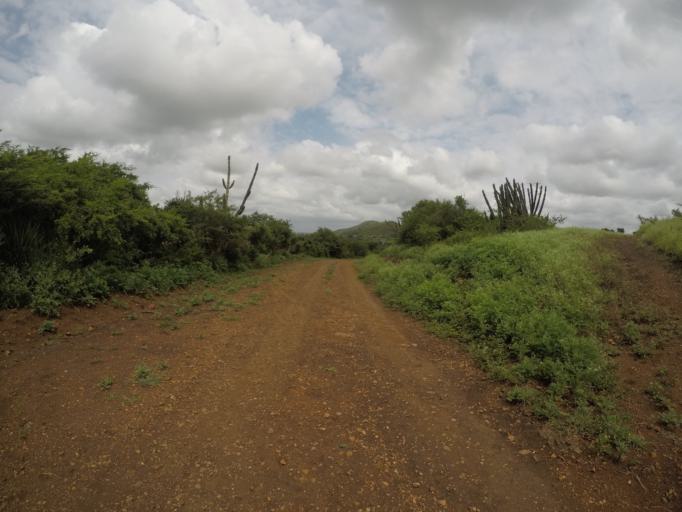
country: ZA
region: KwaZulu-Natal
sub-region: uThungulu District Municipality
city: Empangeni
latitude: -28.5950
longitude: 31.8787
